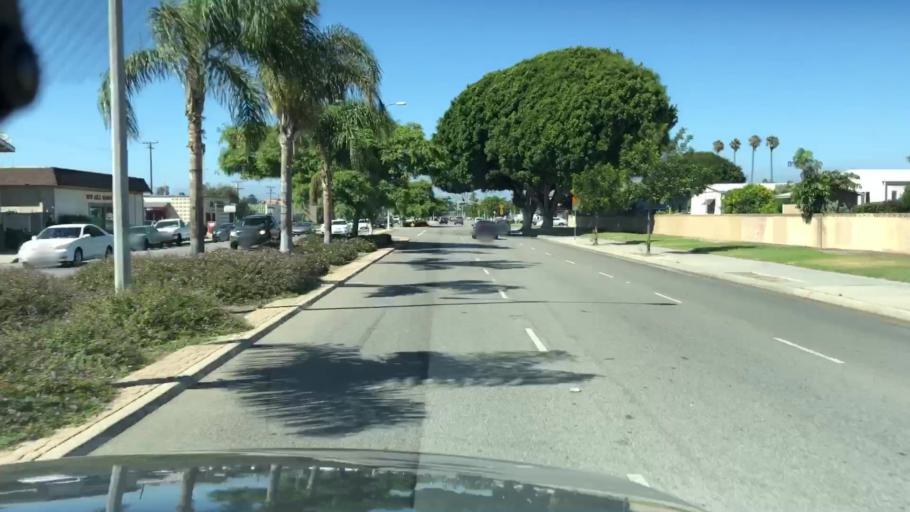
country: US
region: California
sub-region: Ventura County
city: Port Hueneme
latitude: 34.1642
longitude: -119.1776
